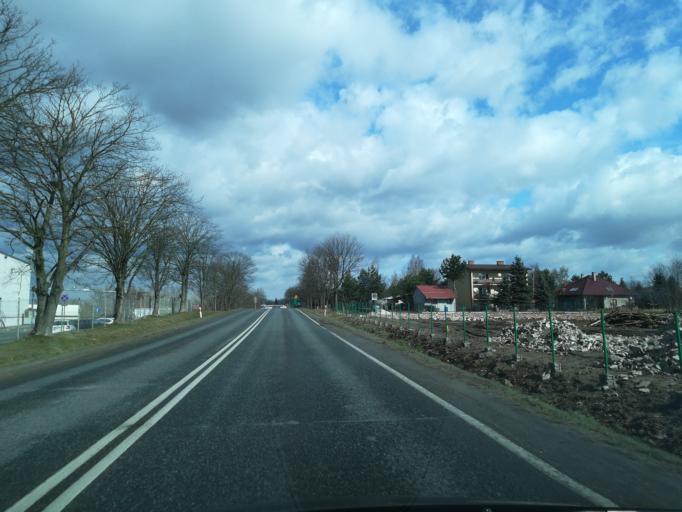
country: PL
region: Lesser Poland Voivodeship
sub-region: Powiat krakowski
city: Kryspinow
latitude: 50.0591
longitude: 19.8034
